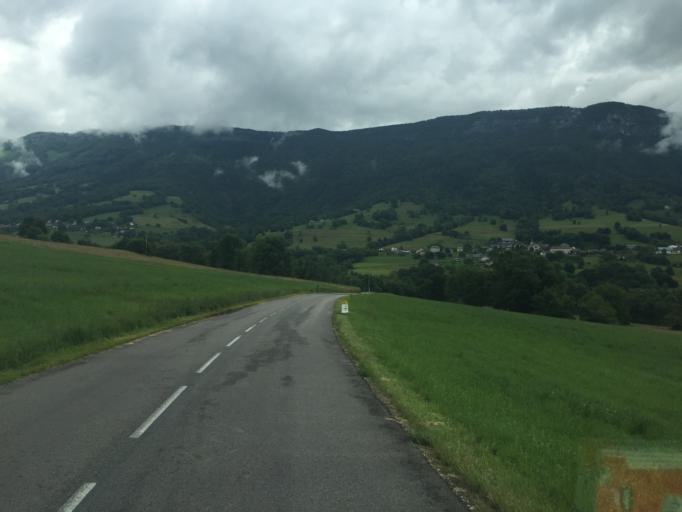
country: FR
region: Rhone-Alpes
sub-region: Departement de la Savoie
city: Barby
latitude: 45.5892
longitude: 6.0138
